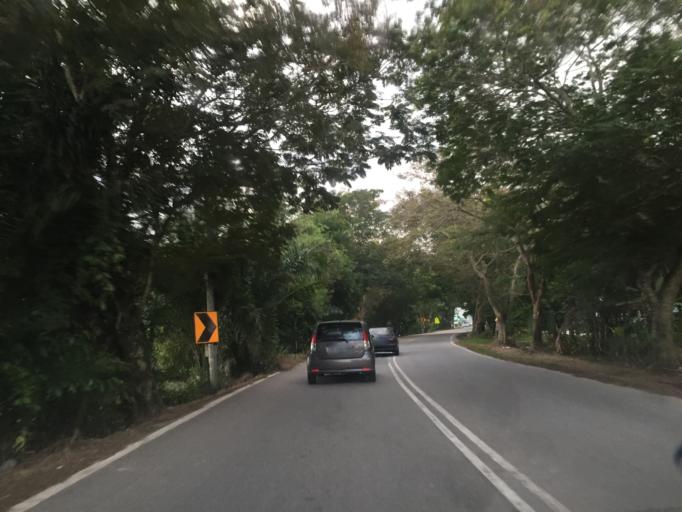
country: MY
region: Penang
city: Tasek Glugor
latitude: 5.5540
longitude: 100.5039
